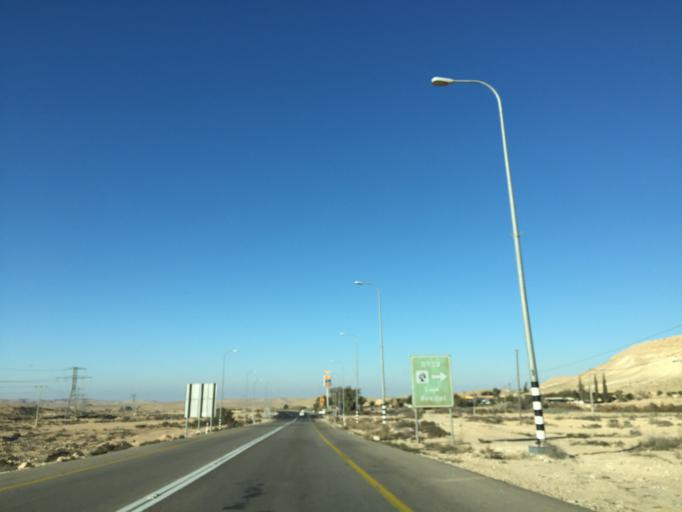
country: IL
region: Southern District
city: Midreshet Ben-Gurion
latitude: 30.7889
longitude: 34.7680
